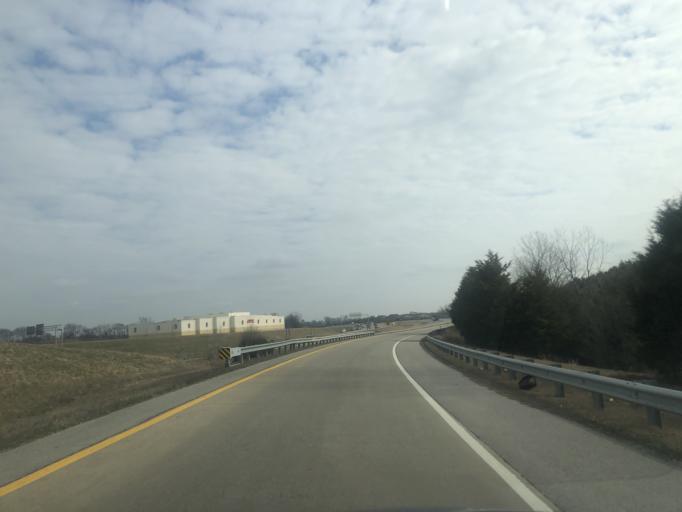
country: US
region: Tennessee
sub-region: Maury County
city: Spring Hill
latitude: 35.7358
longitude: -86.9471
